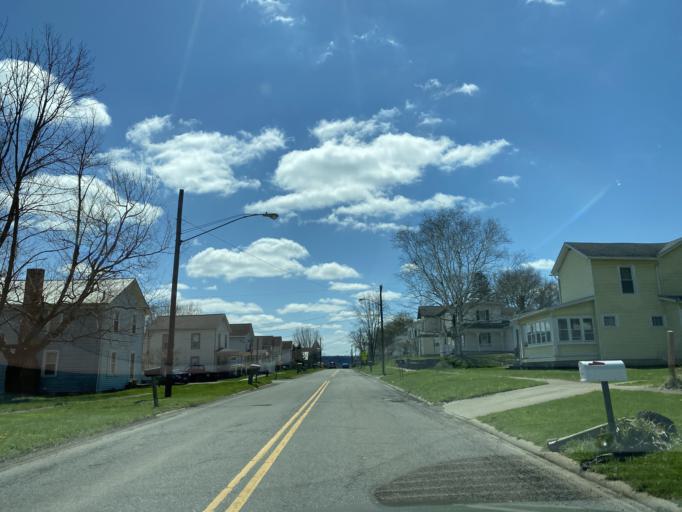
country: US
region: Ohio
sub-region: Wayne County
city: Shreve
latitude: 40.6880
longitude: -82.0223
